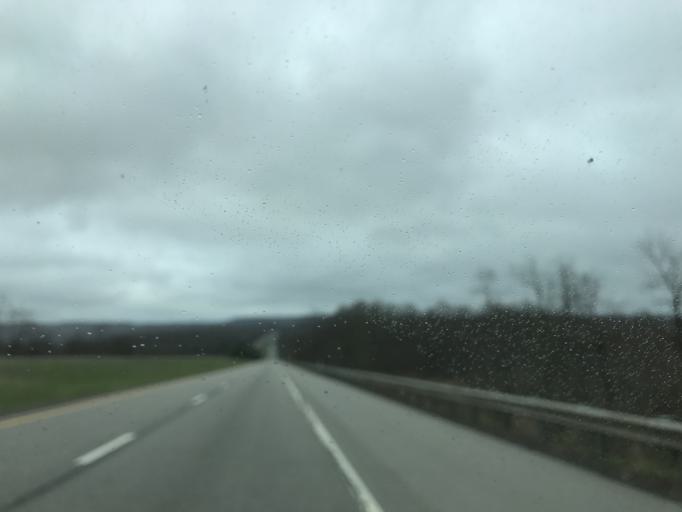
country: US
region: West Virginia
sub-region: Greenbrier County
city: Lewisburg
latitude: 37.8974
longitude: -80.5886
